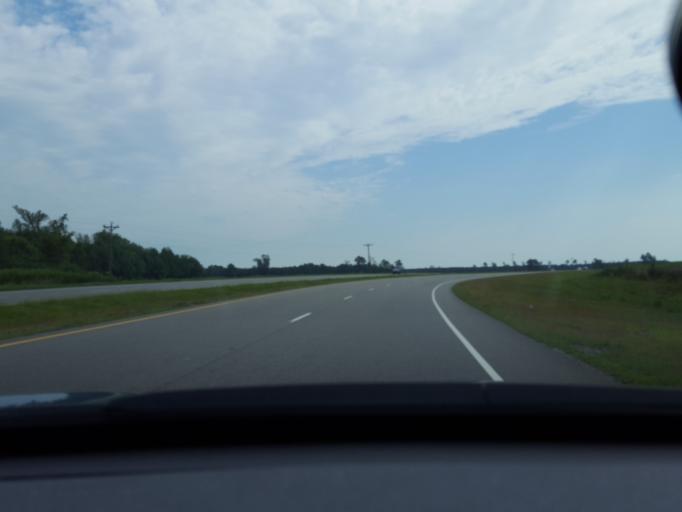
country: US
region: North Carolina
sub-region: Chowan County
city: Edenton
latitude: 36.0392
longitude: -76.7508
